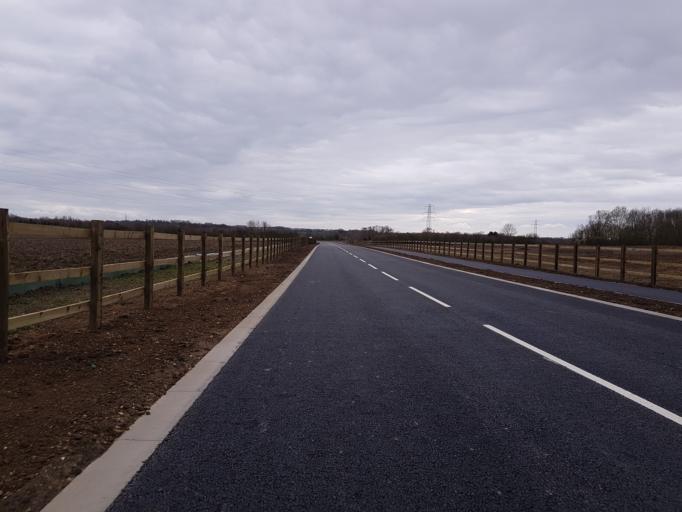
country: GB
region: England
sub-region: Cambridgeshire
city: Girton
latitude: 52.2421
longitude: 0.0496
